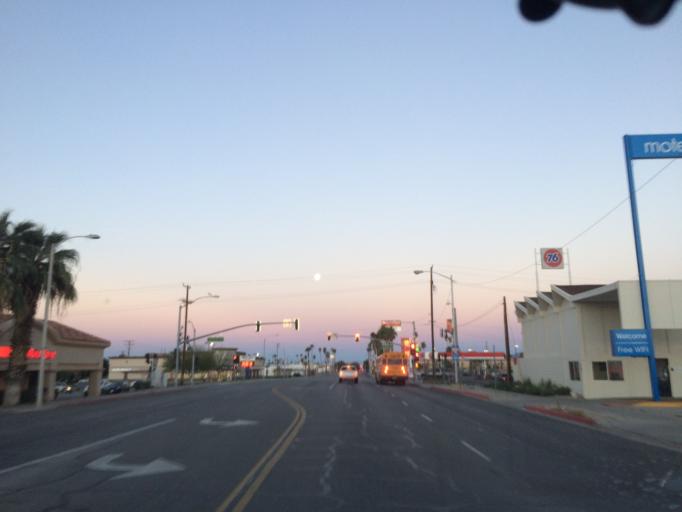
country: US
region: California
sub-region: Riverside County
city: Blythe
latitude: 33.6106
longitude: -114.5872
